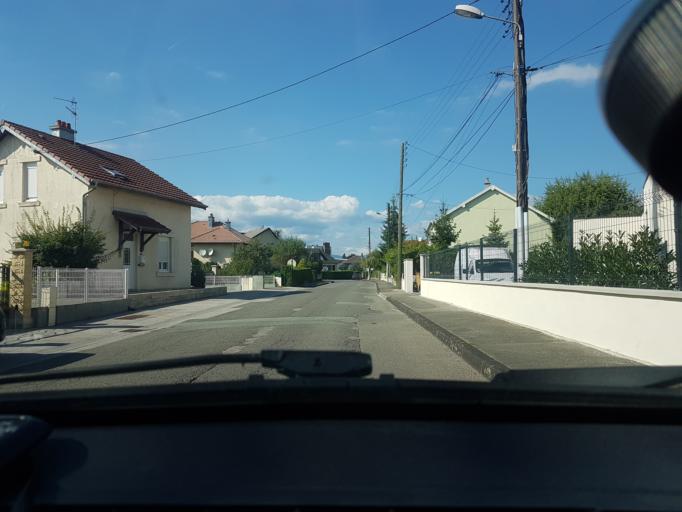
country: FR
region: Franche-Comte
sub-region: Territoire de Belfort
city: Danjoutin
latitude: 47.6126
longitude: 6.8665
